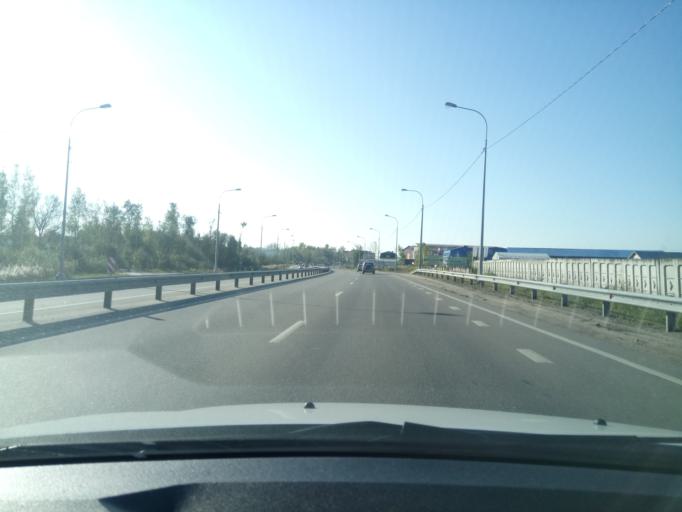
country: RU
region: Nizjnij Novgorod
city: Burevestnik
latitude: 56.1699
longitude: 43.9158
